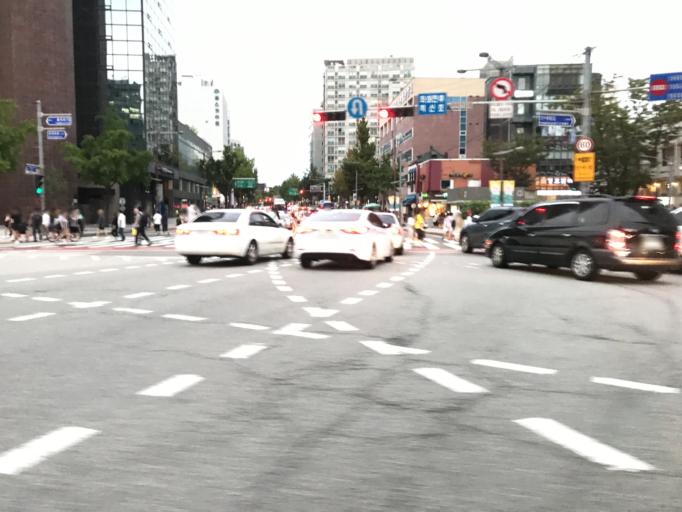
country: KR
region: Seoul
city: Seoul
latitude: 37.5753
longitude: 126.9830
